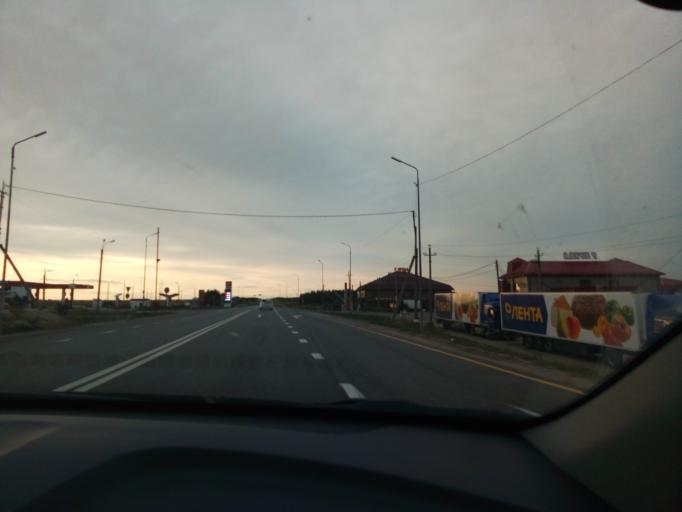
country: RU
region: Volgograd
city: Primorsk
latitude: 49.2653
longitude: 44.8800
